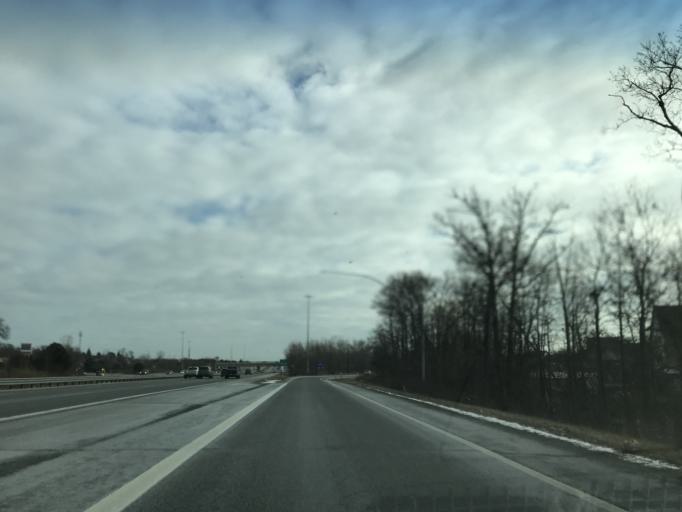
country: US
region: Michigan
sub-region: Oakland County
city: Pontiac
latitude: 42.7049
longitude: -83.3139
